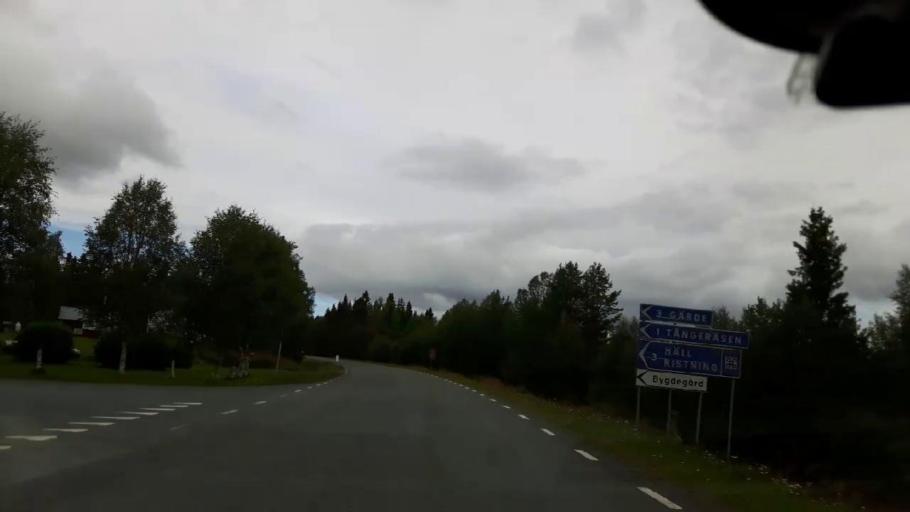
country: SE
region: Jaemtland
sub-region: Krokoms Kommun
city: Valla
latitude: 63.5699
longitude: 13.8394
